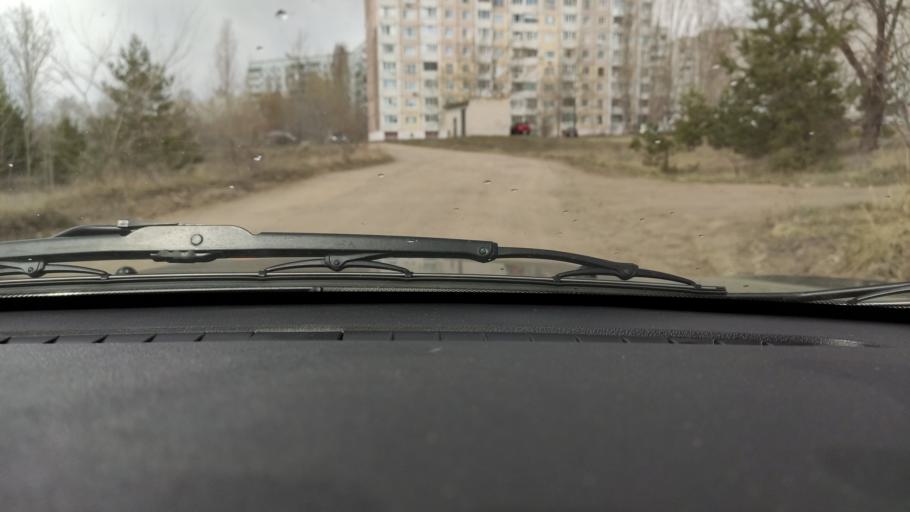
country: RU
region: Voronezj
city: Shilovo
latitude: 51.5572
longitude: 39.1159
